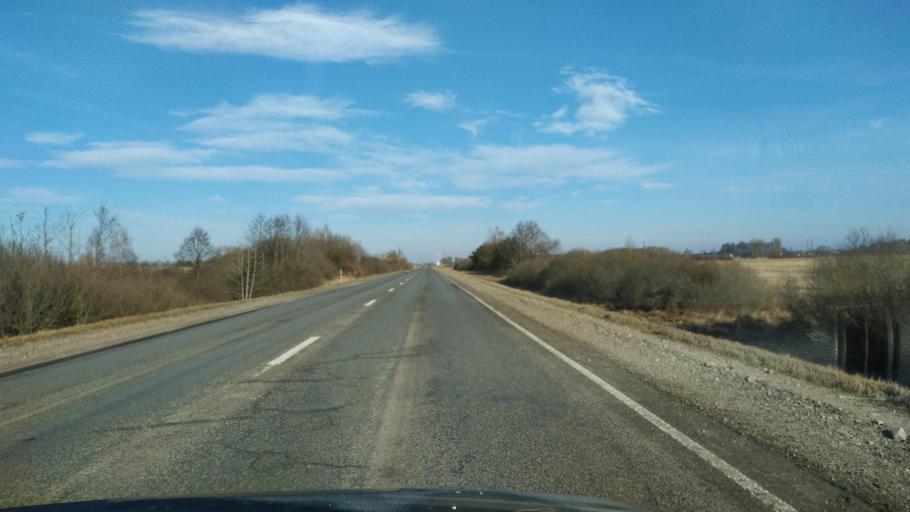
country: BY
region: Brest
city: Kamyanyets
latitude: 52.3914
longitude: 23.7865
